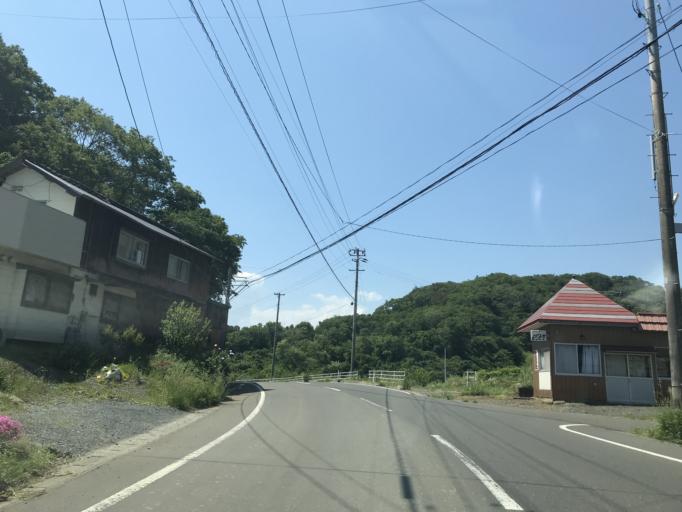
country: JP
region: Miyagi
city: Matsushima
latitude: 38.3355
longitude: 141.1540
